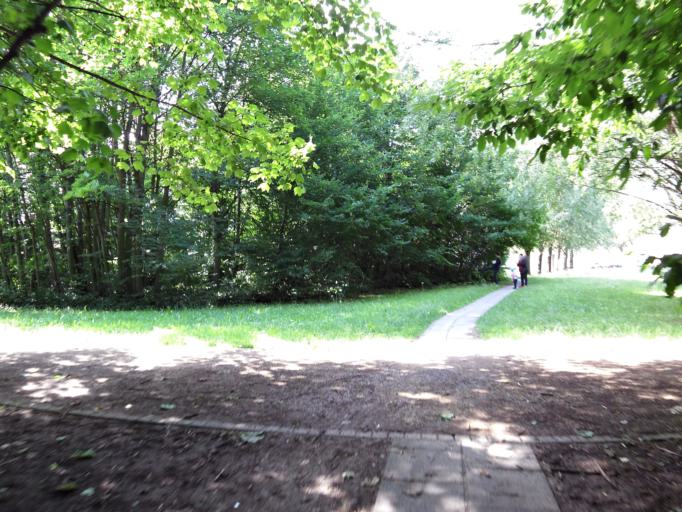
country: DE
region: Saxony
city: Leipzig
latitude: 51.3429
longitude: 12.4175
